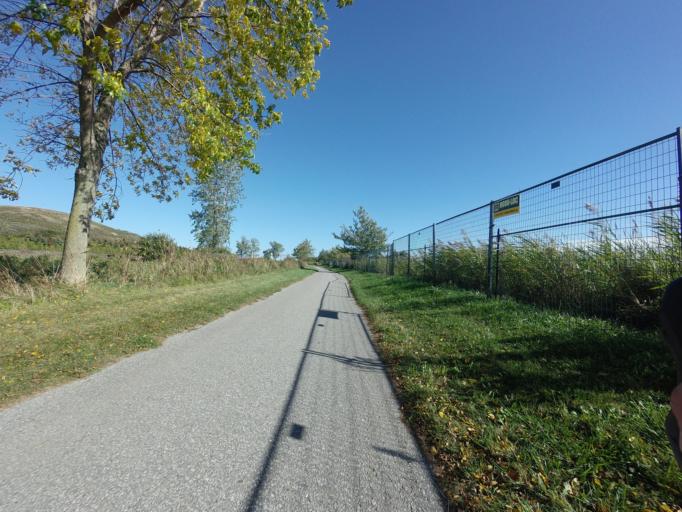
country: CA
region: Ontario
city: Oshawa
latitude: 43.8474
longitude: -78.9108
